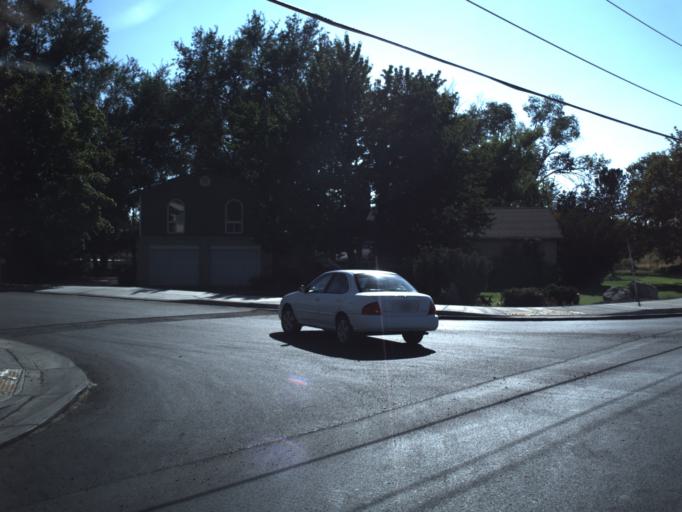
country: US
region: Utah
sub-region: Weber County
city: West Haven
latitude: 41.1907
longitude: -112.0834
